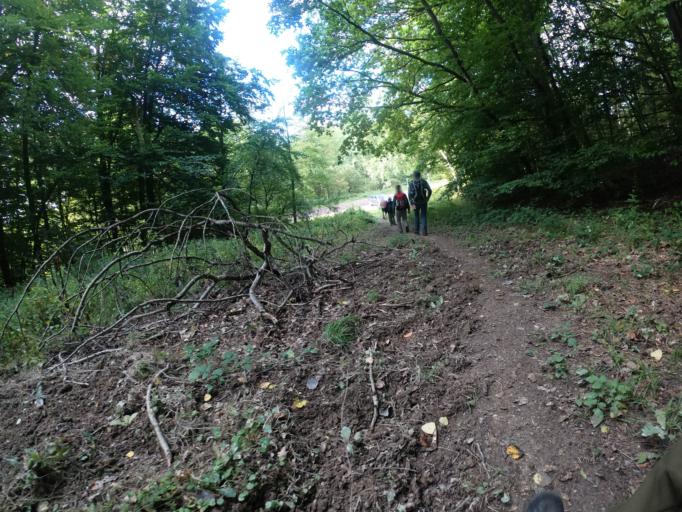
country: DE
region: Hesse
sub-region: Regierungsbezirk Darmstadt
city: Niedernhausen
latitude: 50.1271
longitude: 8.2753
